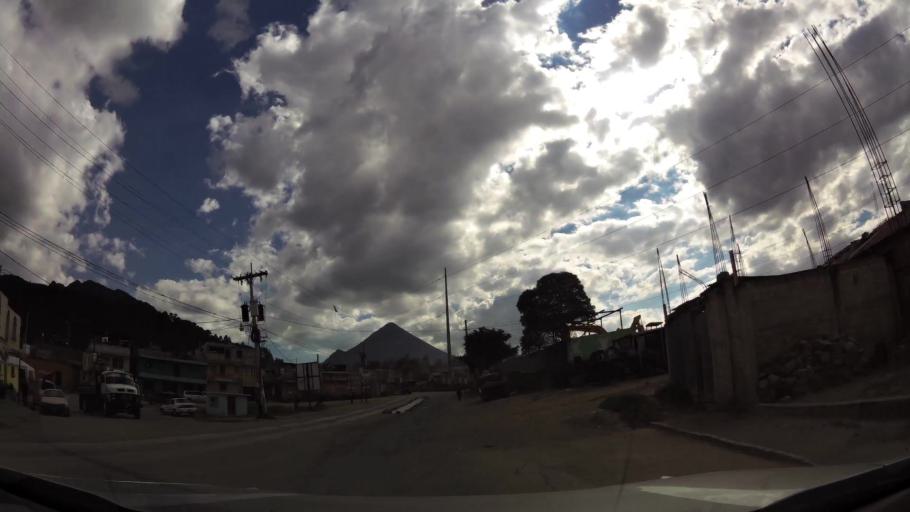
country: GT
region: Quetzaltenango
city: Quetzaltenango
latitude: 14.8294
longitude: -91.5367
